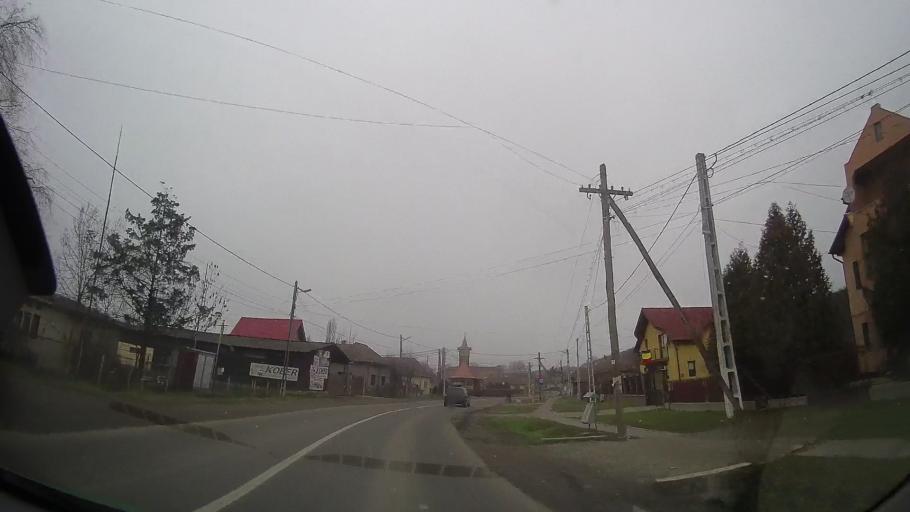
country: RO
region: Mures
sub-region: Comuna Ceausu de Campie
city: Ceausu de Campie
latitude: 46.6411
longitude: 24.5145
